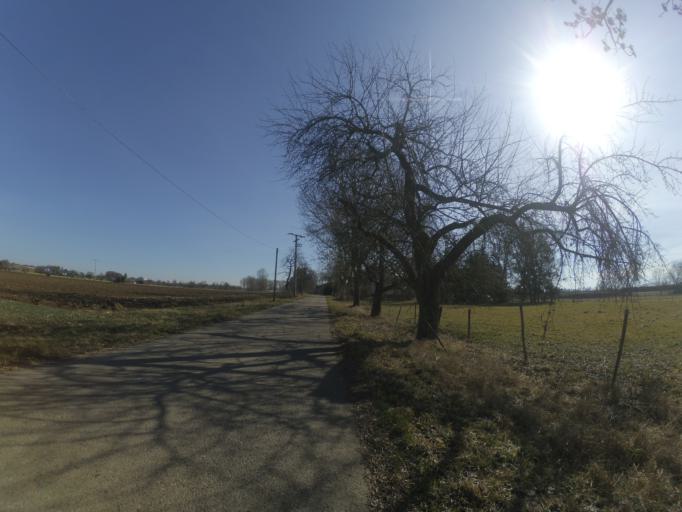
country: DE
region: Baden-Wuerttemberg
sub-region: Tuebingen Region
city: Ollingen
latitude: 48.5018
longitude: 10.1474
